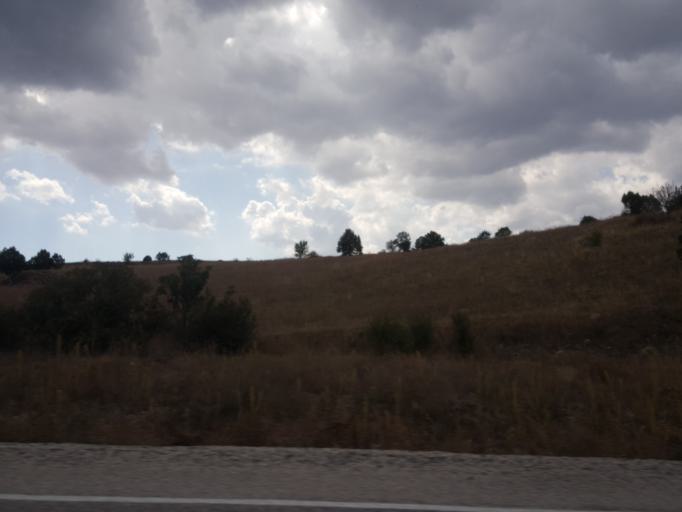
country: TR
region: Yozgat
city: Cekerek
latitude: 40.2018
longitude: 35.5099
